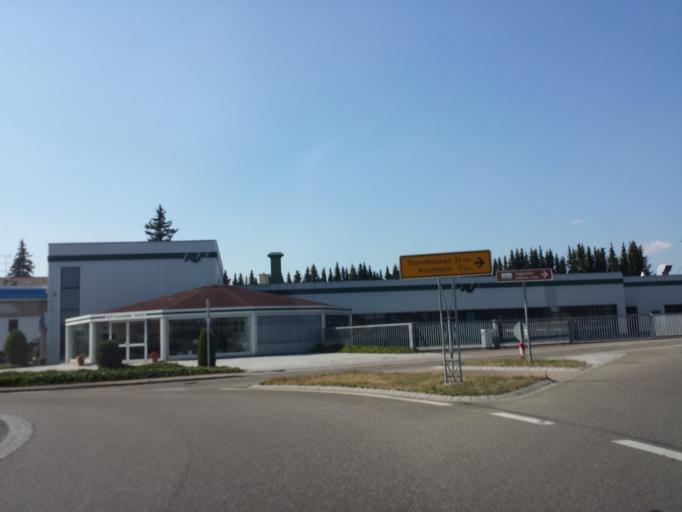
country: DE
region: Bavaria
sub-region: Swabia
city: Pfaffenhausen
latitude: 48.1203
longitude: 10.4629
